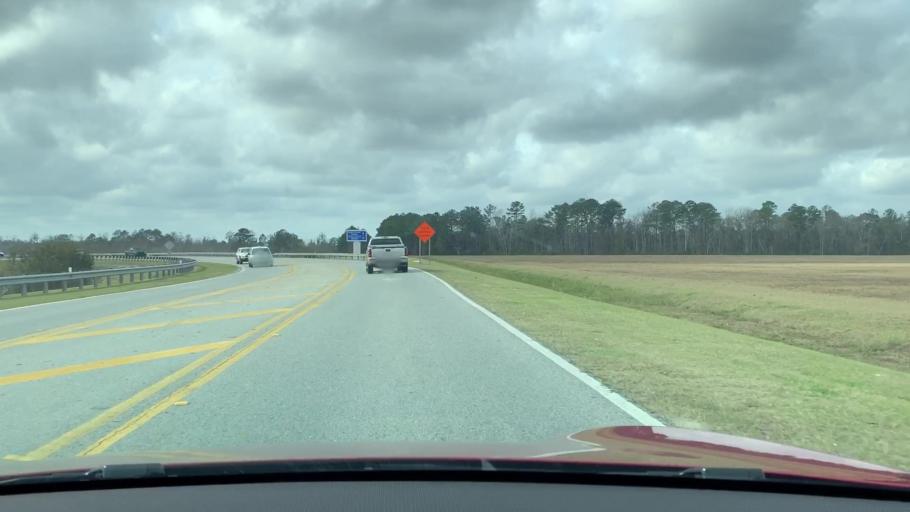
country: US
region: Georgia
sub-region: Chatham County
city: Port Wentworth
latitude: 32.1422
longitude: -81.2083
